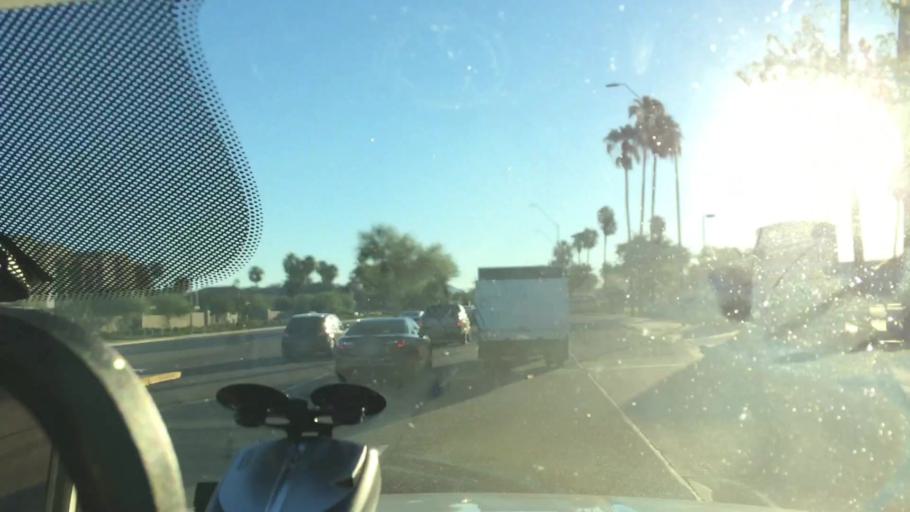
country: US
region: Arizona
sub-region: Maricopa County
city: Paradise Valley
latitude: 33.6402
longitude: -112.0587
